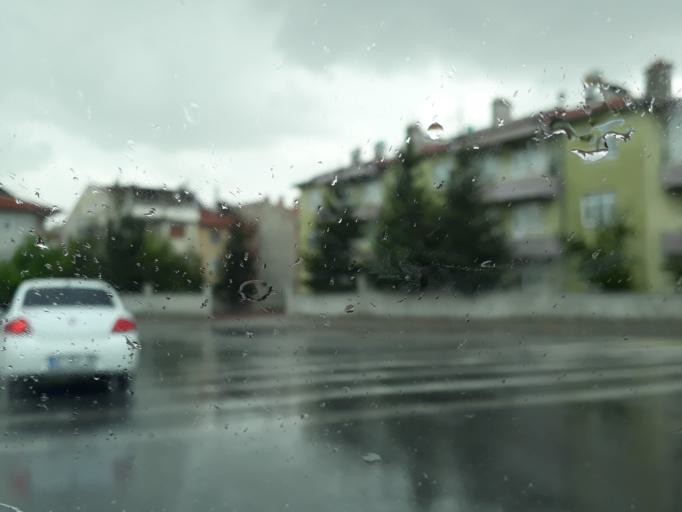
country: TR
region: Konya
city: Selcuklu
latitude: 37.9154
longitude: 32.4922
